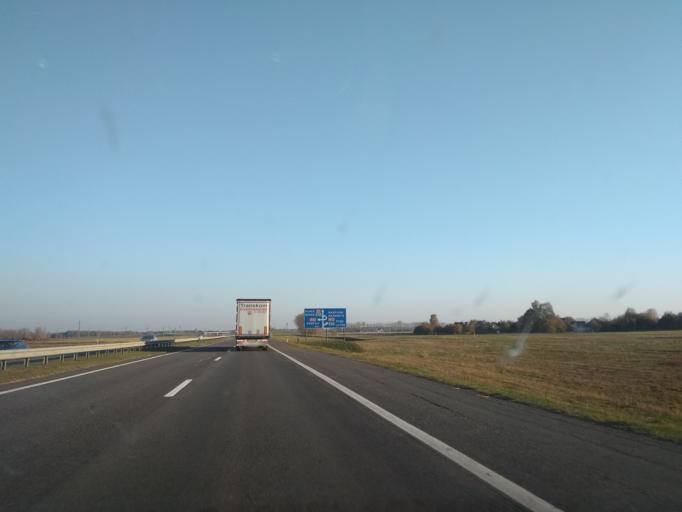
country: BY
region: Brest
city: Kobryn
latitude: 52.1905
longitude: 24.3112
